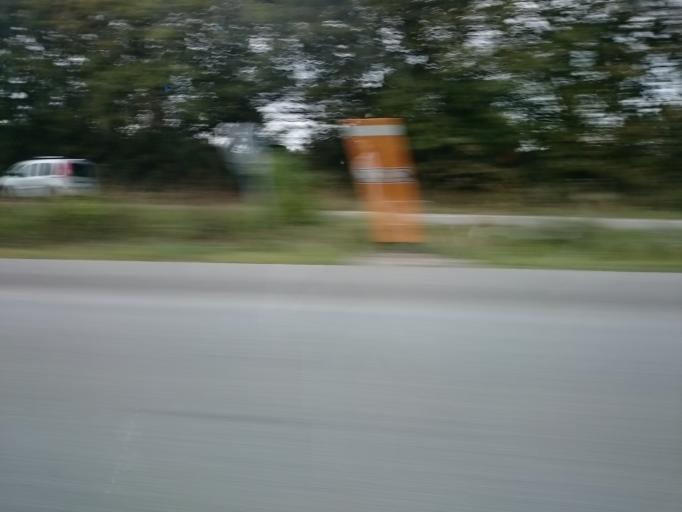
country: FR
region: Brittany
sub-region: Departement du Morbihan
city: Landaul
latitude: 47.7177
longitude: -3.0613
